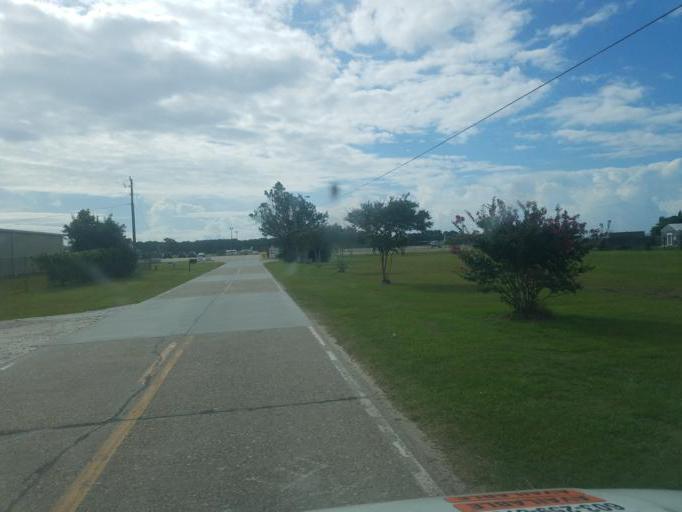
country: US
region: North Carolina
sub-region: Dare County
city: Manteo
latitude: 35.9180
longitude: -75.7028
